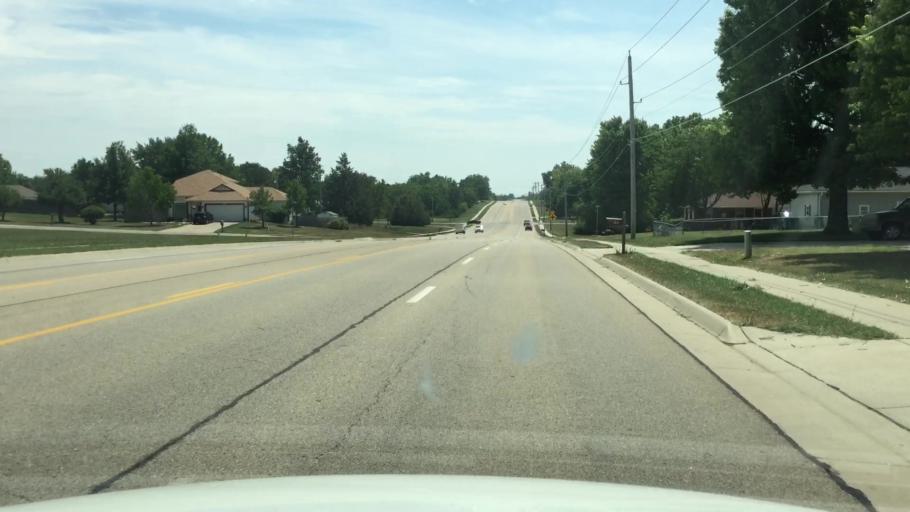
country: US
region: Kansas
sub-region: Shawnee County
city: Topeka
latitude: 39.0033
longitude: -95.6145
